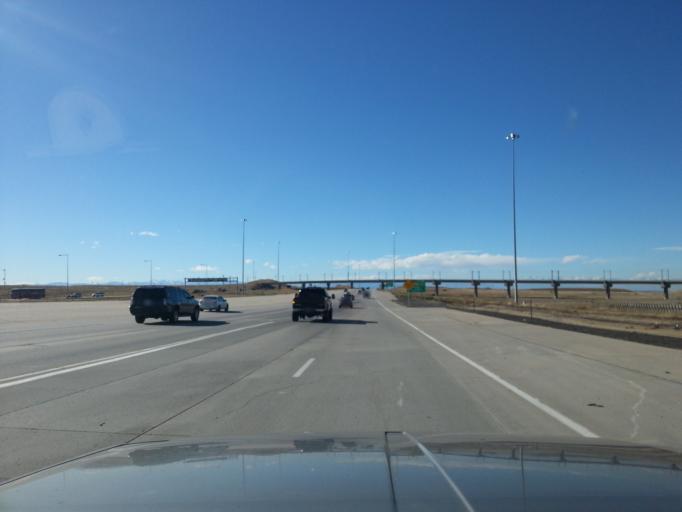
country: US
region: Colorado
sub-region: Adams County
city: Aurora
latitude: 39.8346
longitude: -104.7280
